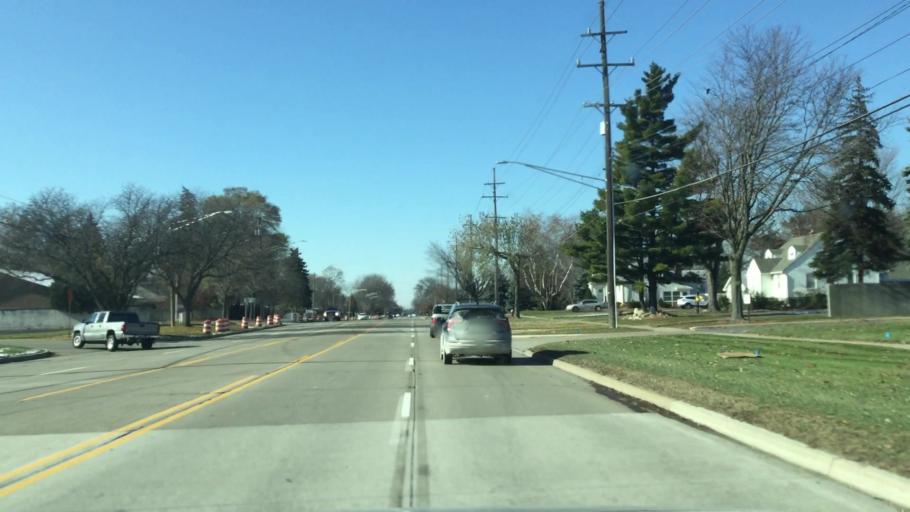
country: US
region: Michigan
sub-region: Oakland County
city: Madison Heights
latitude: 42.5204
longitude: -83.0689
